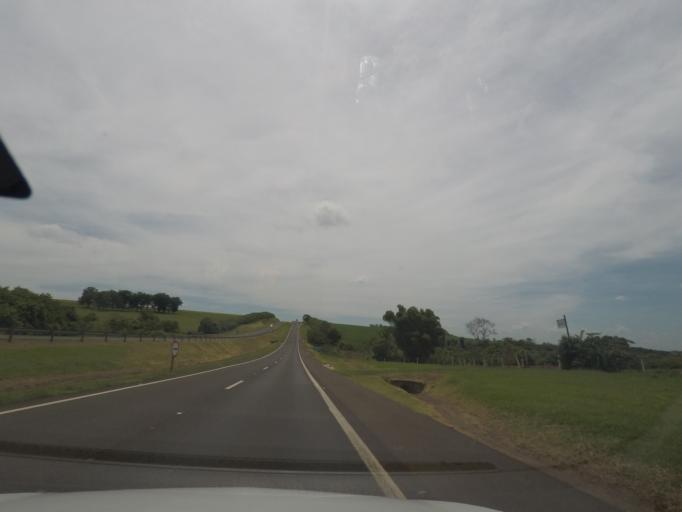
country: BR
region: Sao Paulo
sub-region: Bebedouro
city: Bebedouro
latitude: -21.0169
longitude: -48.4252
